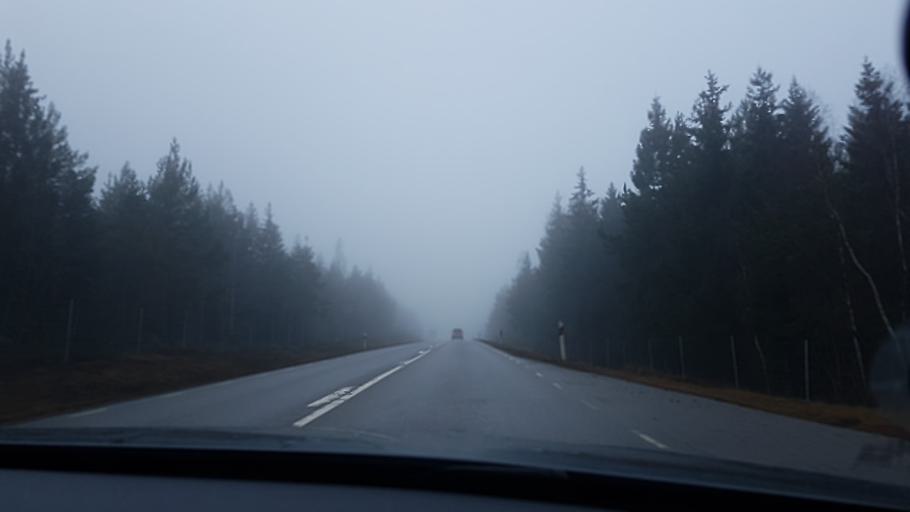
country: SE
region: Vaestra Goetaland
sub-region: Gullspangs Kommun
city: Gullspang
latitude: 58.9561
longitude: 14.0565
